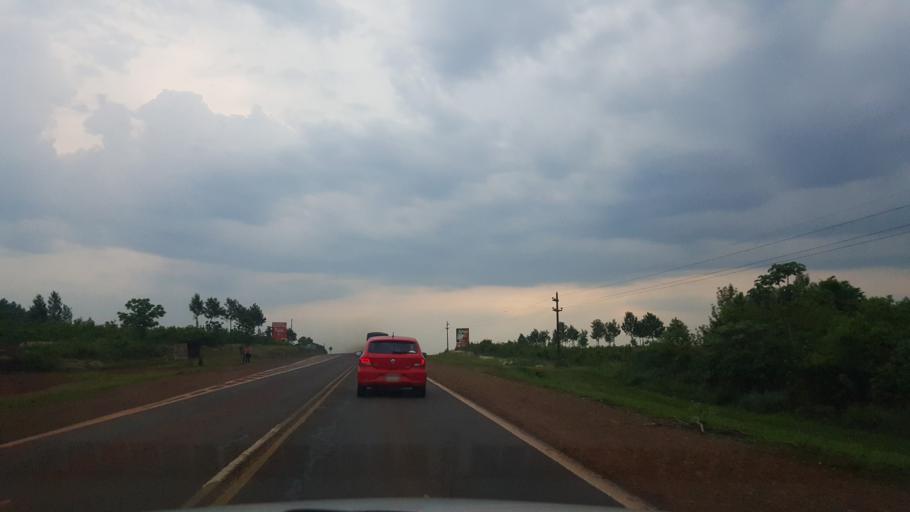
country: AR
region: Misiones
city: Gobernador Roca
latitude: -27.1666
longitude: -55.4413
